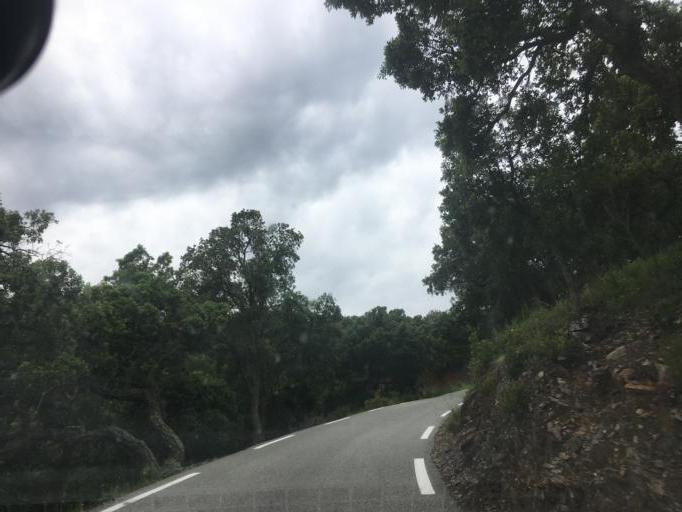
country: FR
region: Provence-Alpes-Cote d'Azur
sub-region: Departement du Var
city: Pierrefeu-du-Var
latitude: 43.2185
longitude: 6.2189
